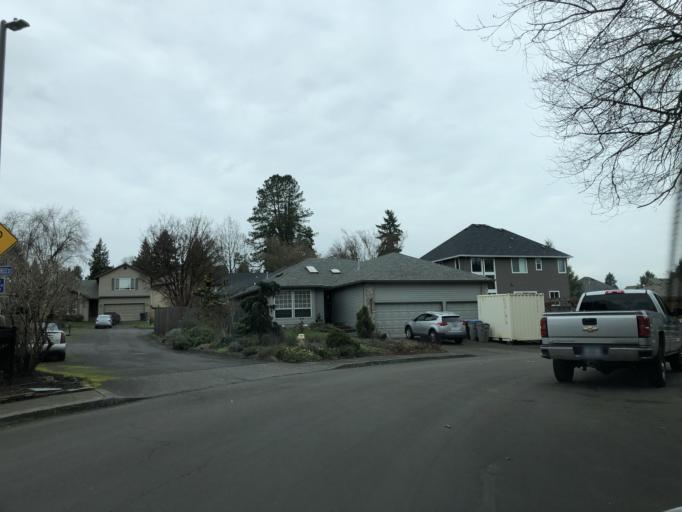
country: US
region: Oregon
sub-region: Washington County
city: Tigard
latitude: 45.4162
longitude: -122.7745
